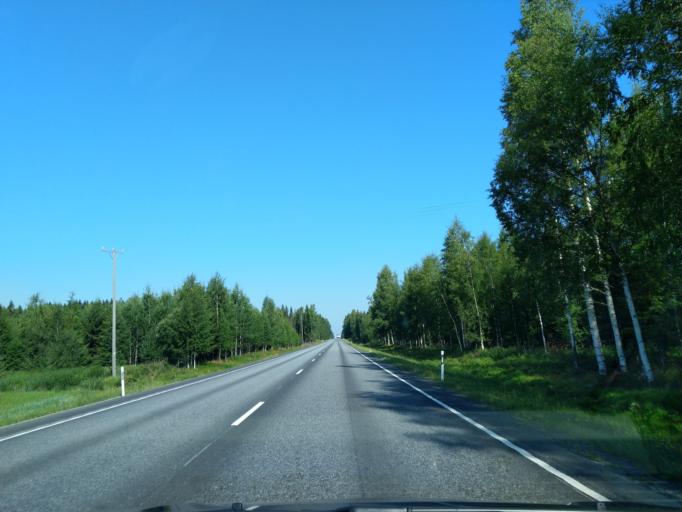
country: FI
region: Varsinais-Suomi
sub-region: Loimaa
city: Alastaro
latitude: 61.0700
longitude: 22.9228
